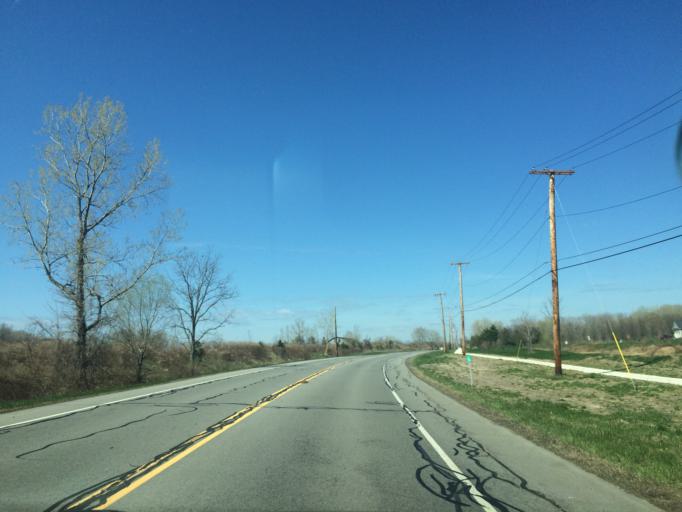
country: US
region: New York
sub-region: Monroe County
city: Fairport
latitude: 43.0945
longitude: -77.3770
